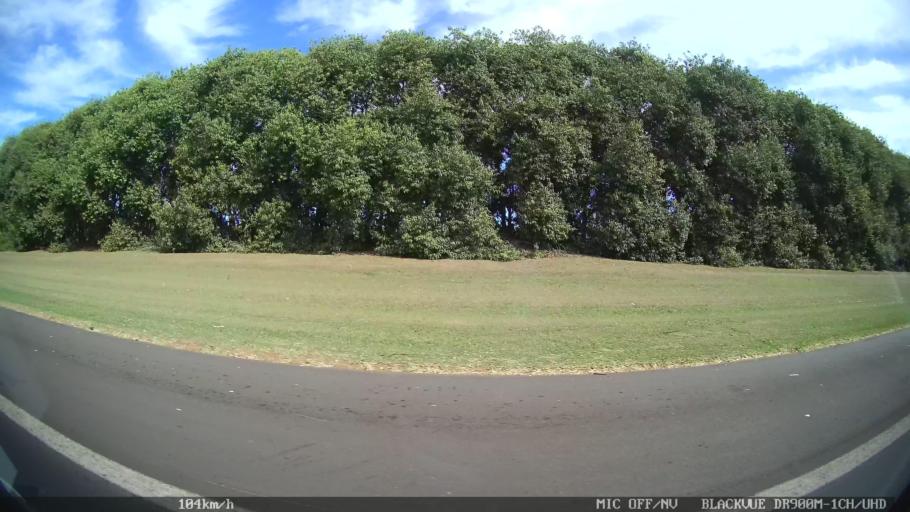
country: BR
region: Sao Paulo
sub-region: Matao
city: Matao
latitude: -21.6680
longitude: -48.3652
